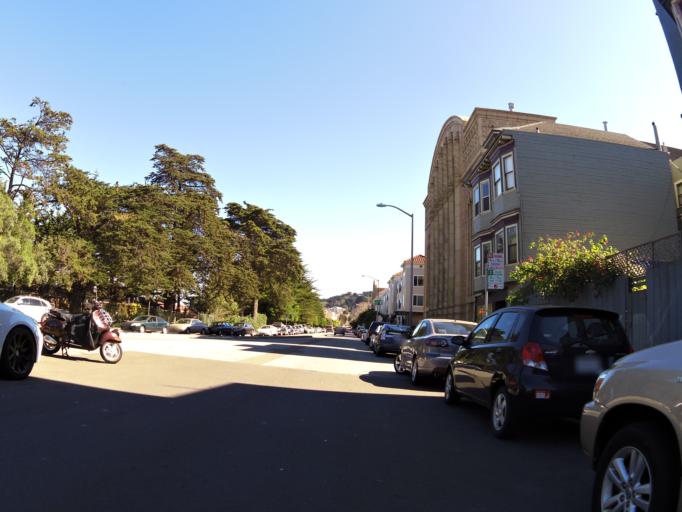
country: US
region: California
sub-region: San Francisco County
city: San Francisco
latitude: 37.7658
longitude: -122.4576
